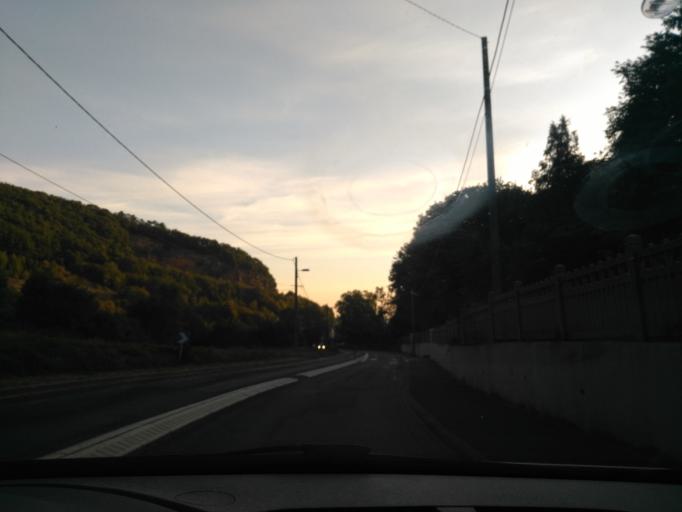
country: FR
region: Rhone-Alpes
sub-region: Departement du Rhone
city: Albigny-sur-Saone
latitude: 45.8658
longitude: 4.8137
